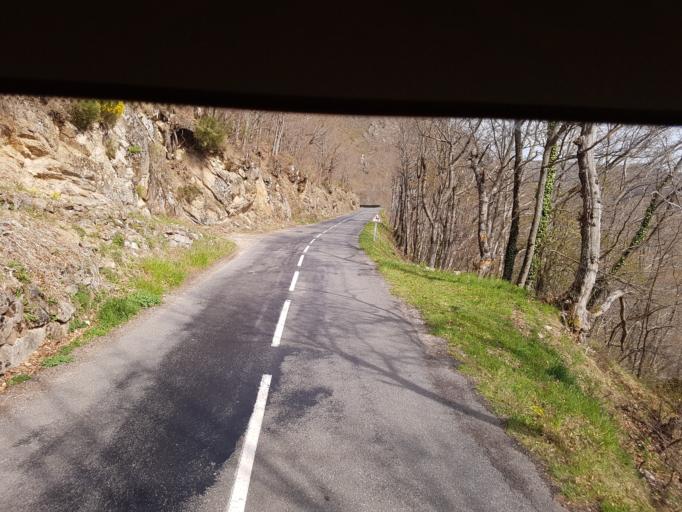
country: FR
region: Languedoc-Roussillon
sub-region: Departement de la Lozere
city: Florac
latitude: 44.3669
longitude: 3.7033
